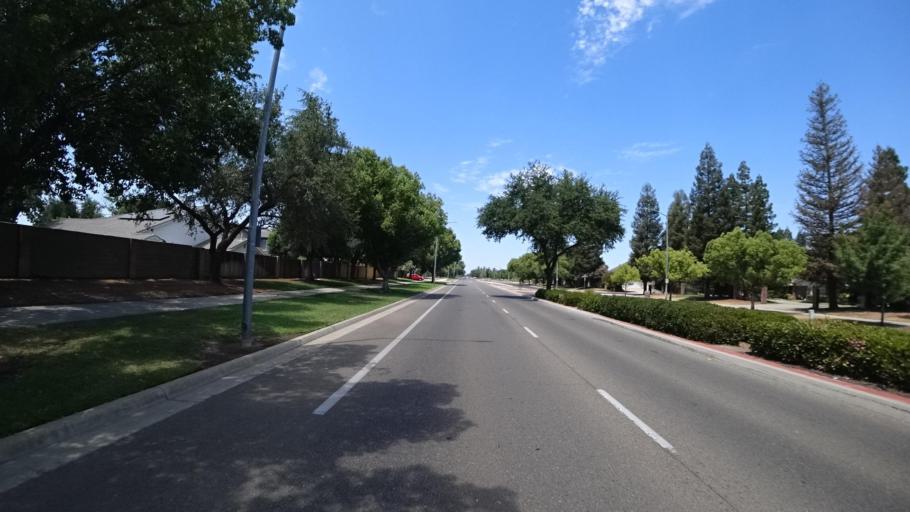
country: US
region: California
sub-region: Fresno County
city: Tarpey Village
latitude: 36.7938
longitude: -119.6666
